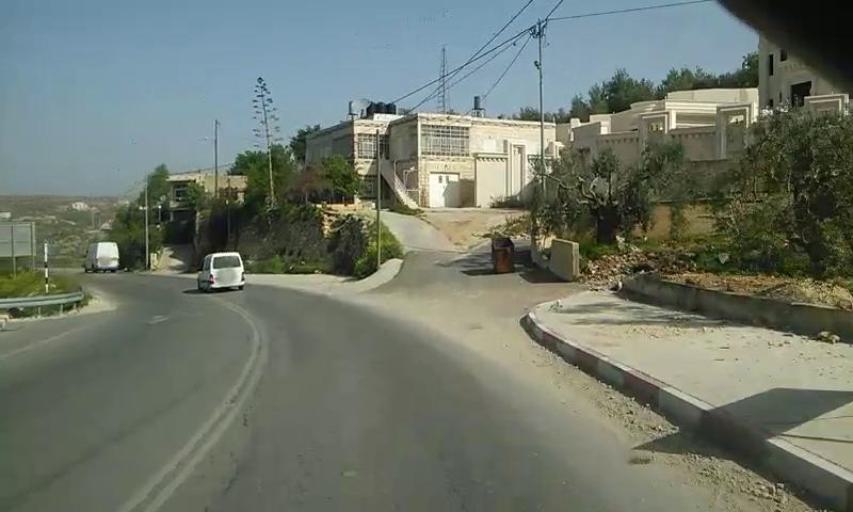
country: PS
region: West Bank
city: Dura al Qar`
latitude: 31.9590
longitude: 35.2258
